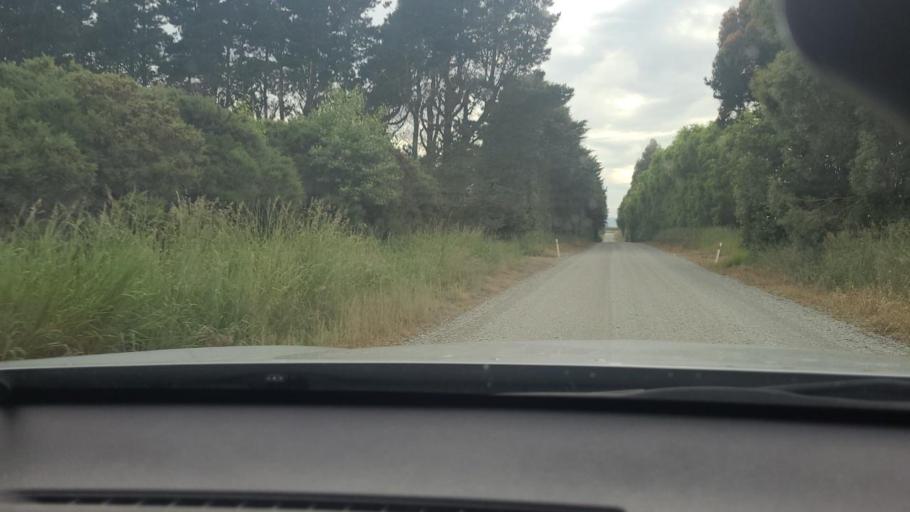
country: NZ
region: Southland
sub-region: Southland District
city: Winton
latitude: -46.2268
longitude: 168.3320
